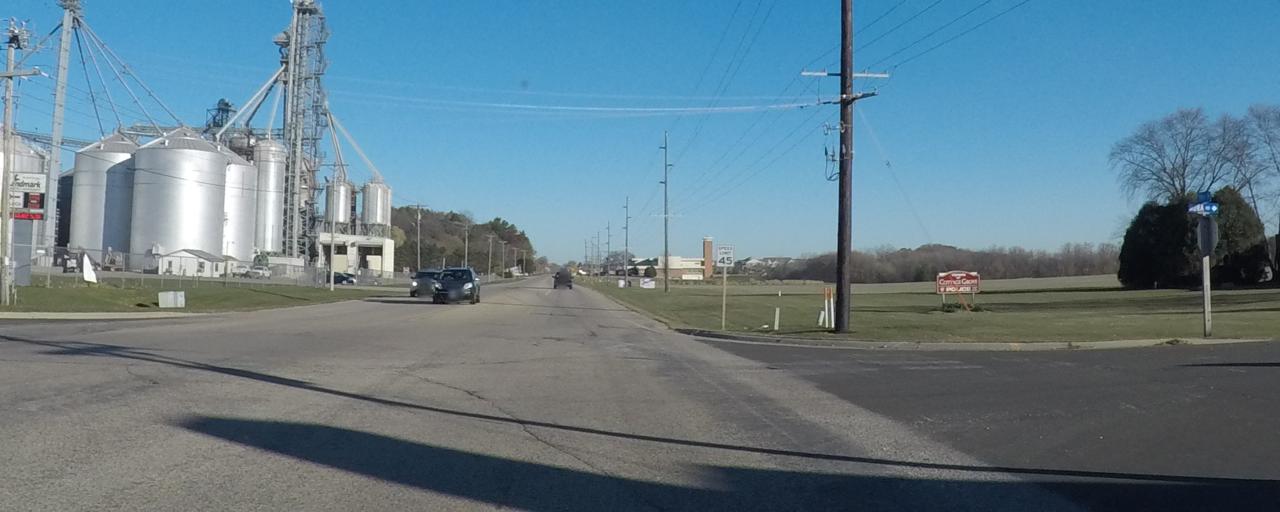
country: US
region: Wisconsin
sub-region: Dane County
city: Cottage Grove
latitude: 43.0649
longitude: -89.1996
